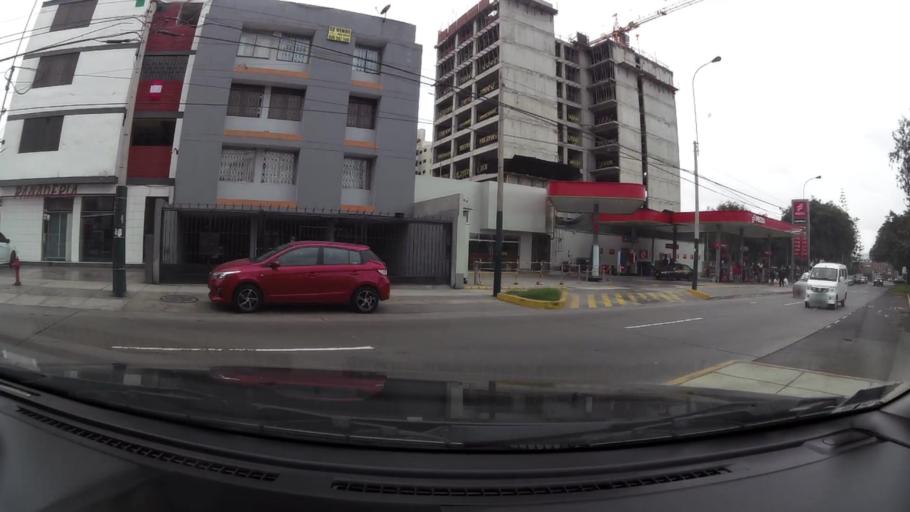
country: PE
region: Lima
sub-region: Lima
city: Surco
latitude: -12.1418
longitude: -77.0017
